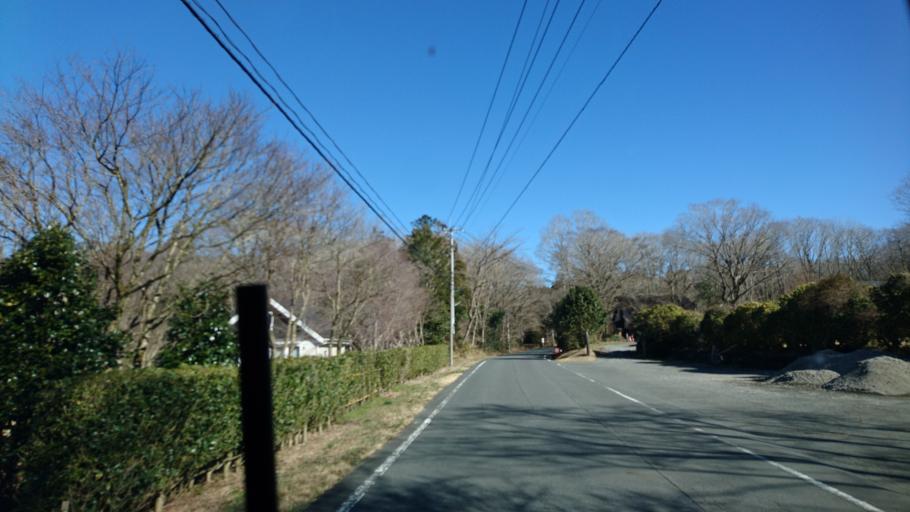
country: JP
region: Shizuoka
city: Fujinomiya
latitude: 35.3535
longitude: 138.5714
